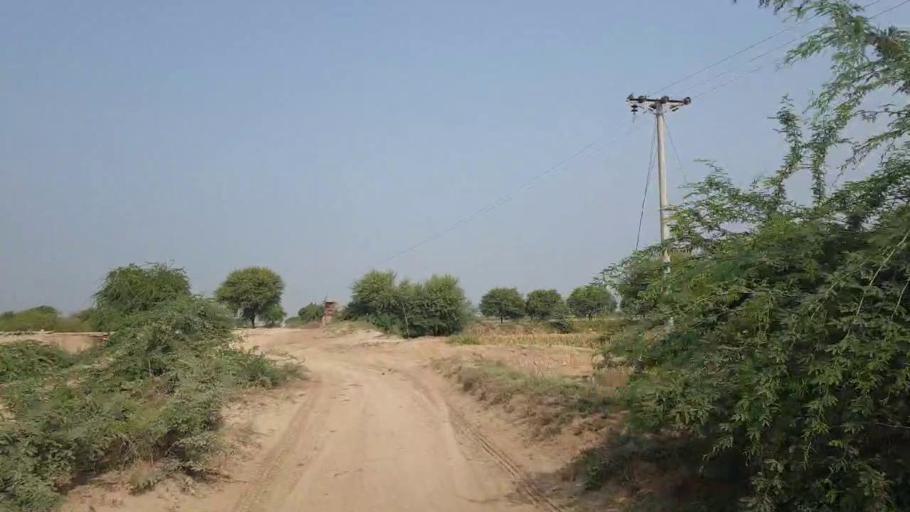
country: PK
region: Sindh
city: Badin
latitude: 24.6994
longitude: 68.7775
